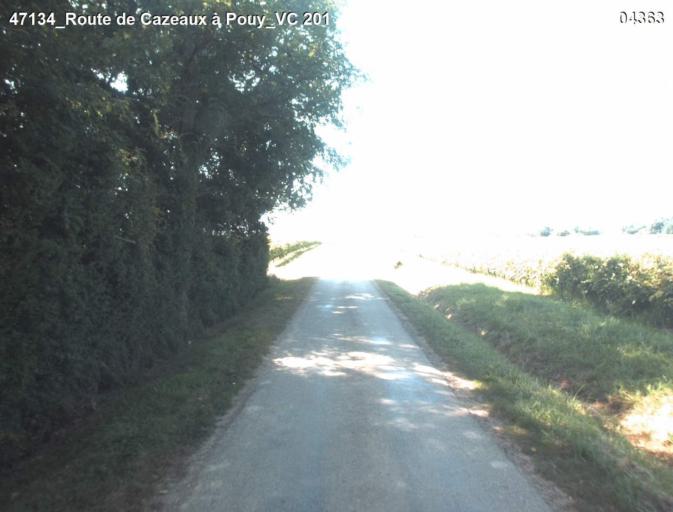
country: FR
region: Aquitaine
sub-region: Departement du Lot-et-Garonne
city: Mezin
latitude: 44.0352
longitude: 0.3119
